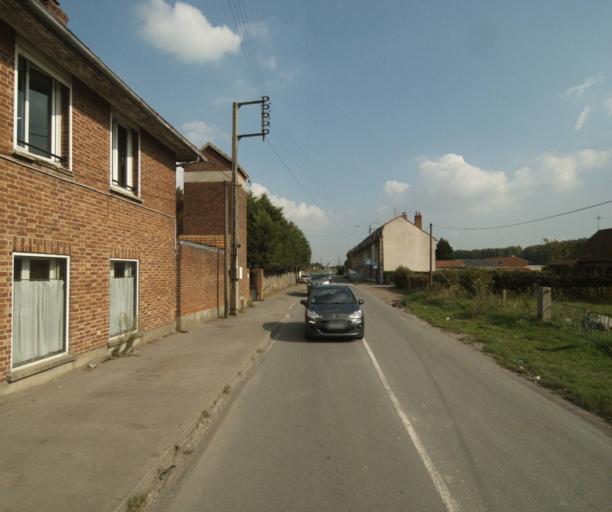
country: FR
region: Nord-Pas-de-Calais
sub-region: Departement du Nord
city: Santes
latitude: 50.5695
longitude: 2.9693
